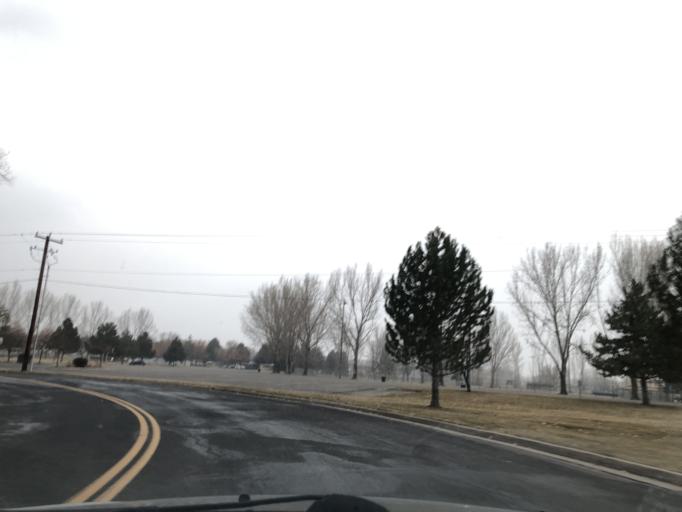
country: US
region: Utah
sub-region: Cache County
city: Logan
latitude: 41.7191
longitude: -111.8491
